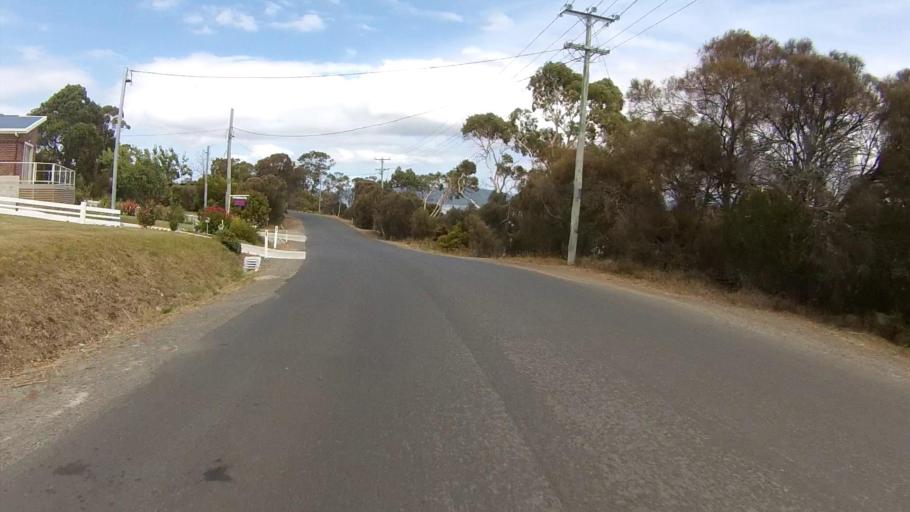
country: AU
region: Tasmania
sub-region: Kingborough
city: Margate
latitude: -43.0250
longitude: 147.2908
